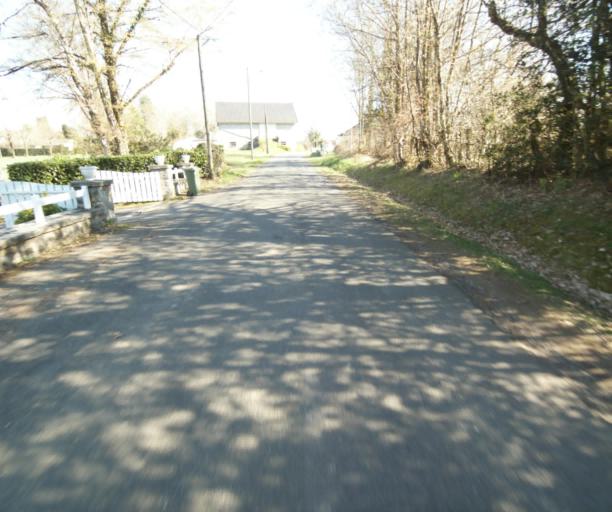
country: FR
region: Limousin
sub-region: Departement de la Correze
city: Tulle
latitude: 45.2810
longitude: 1.7189
